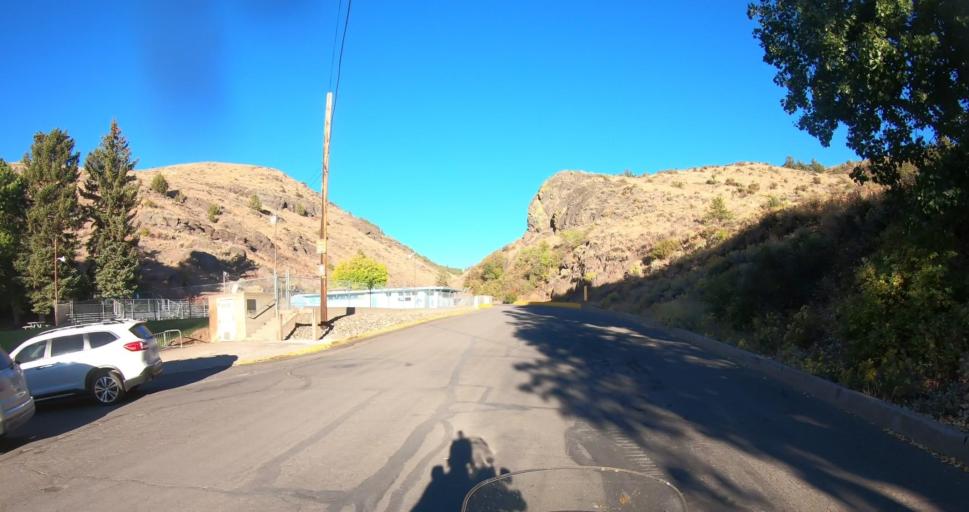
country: US
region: Oregon
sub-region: Lake County
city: Lakeview
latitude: 42.1895
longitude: -120.3430
